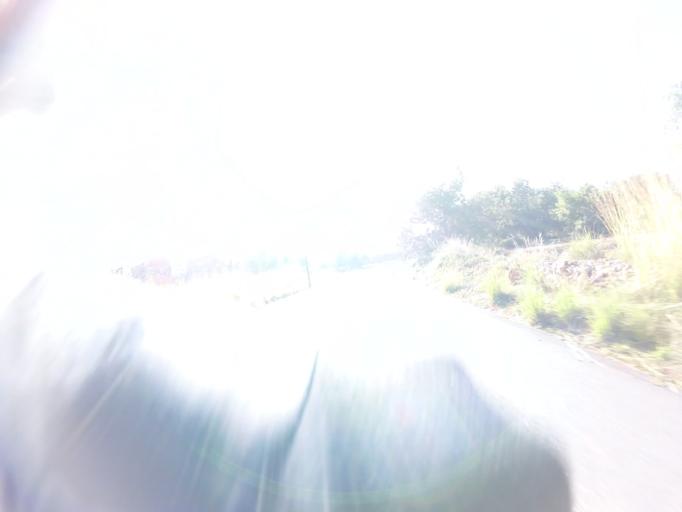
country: ES
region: Valencia
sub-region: Provincia de Castello
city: Peniscola
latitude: 40.3868
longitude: 0.3778
